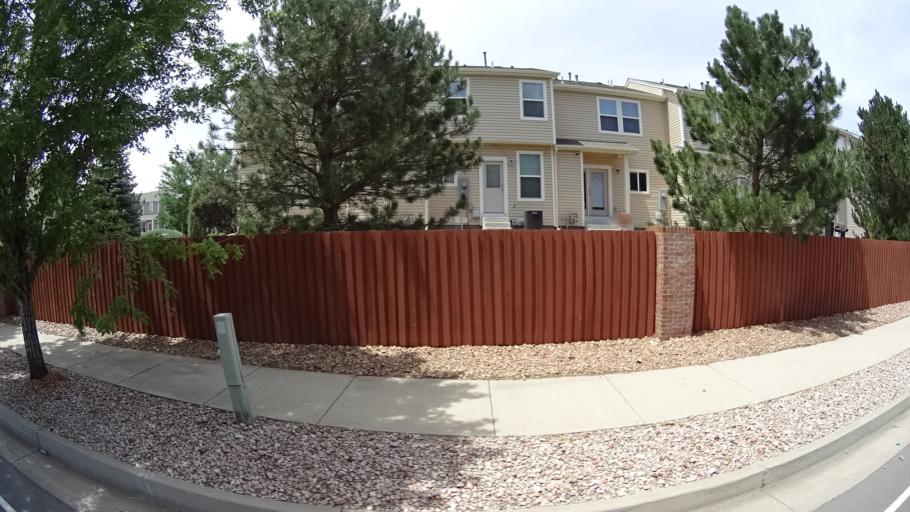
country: US
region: Colorado
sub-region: El Paso County
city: Fountain
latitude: 38.6779
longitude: -104.6875
